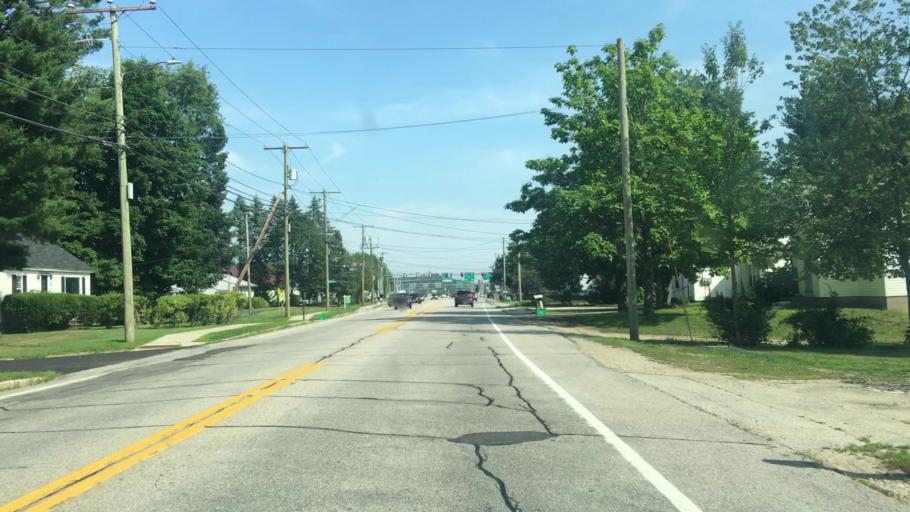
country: US
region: New Hampshire
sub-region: Strafford County
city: Dover
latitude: 43.2252
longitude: -70.8918
